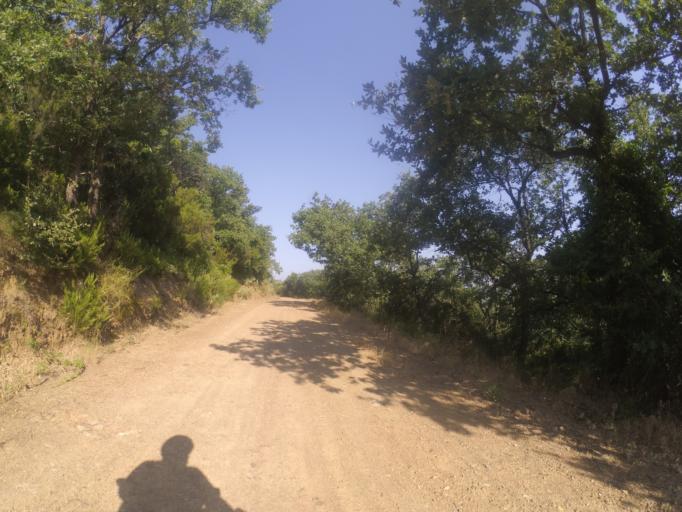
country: FR
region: Languedoc-Roussillon
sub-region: Departement des Pyrenees-Orientales
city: Ille-sur-Tet
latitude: 42.6523
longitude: 2.6460
